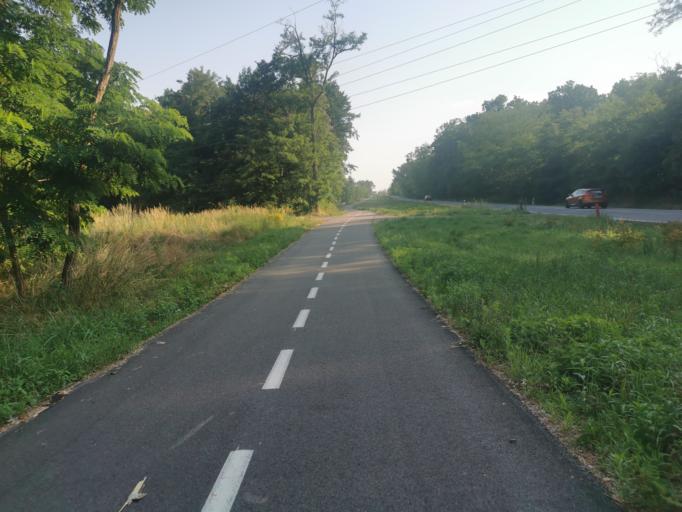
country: CZ
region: South Moravian
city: Ratiskovice
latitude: 48.8926
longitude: 17.1526
